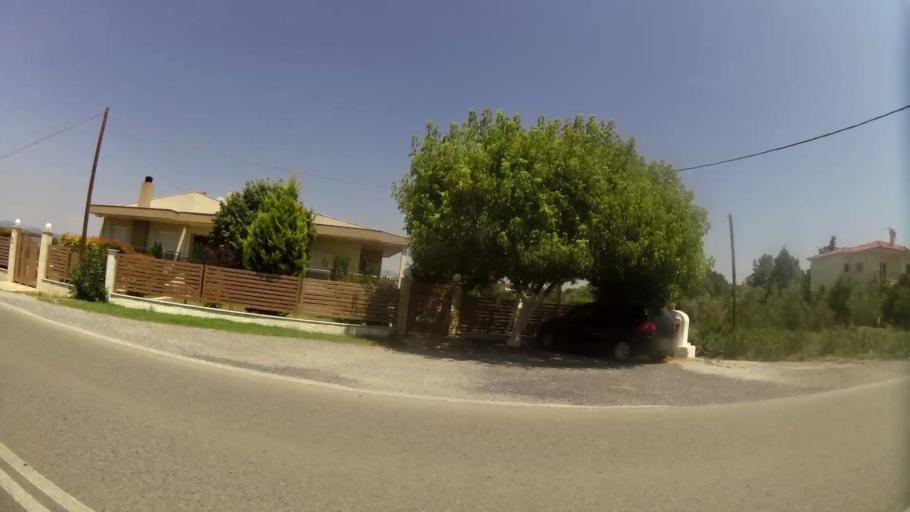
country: GR
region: Central Macedonia
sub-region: Nomos Thessalonikis
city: Trilofos
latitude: 40.4704
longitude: 22.9744
